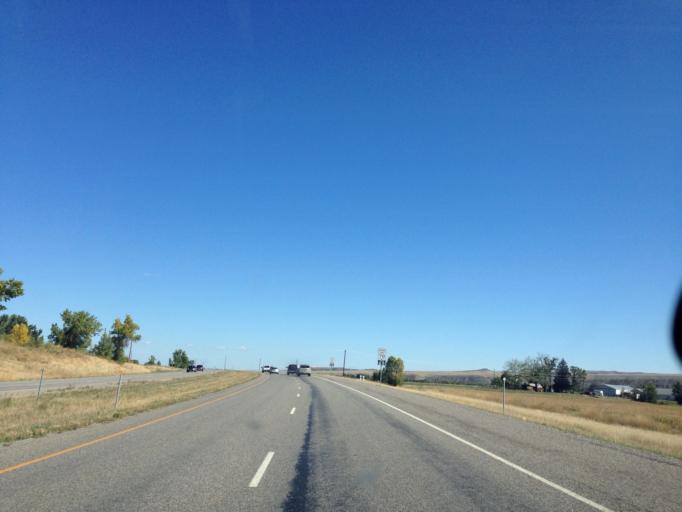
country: US
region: Montana
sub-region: Yellowstone County
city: Laurel
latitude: 45.5248
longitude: -108.8552
